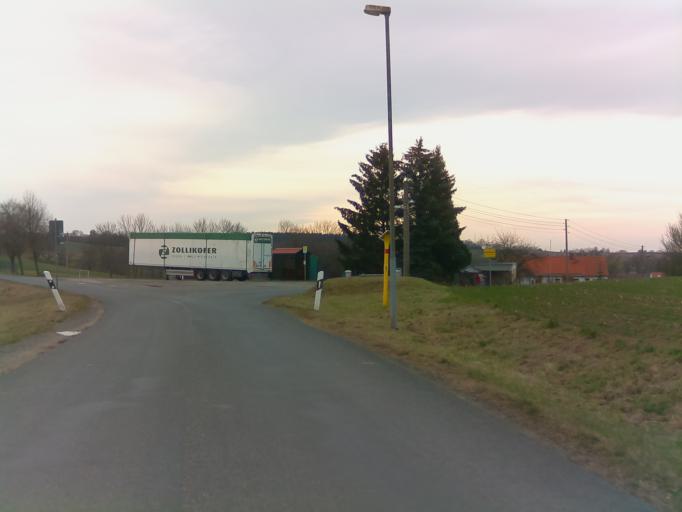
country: DE
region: Thuringia
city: Hundhaupten
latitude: 50.8346
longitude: 11.9953
